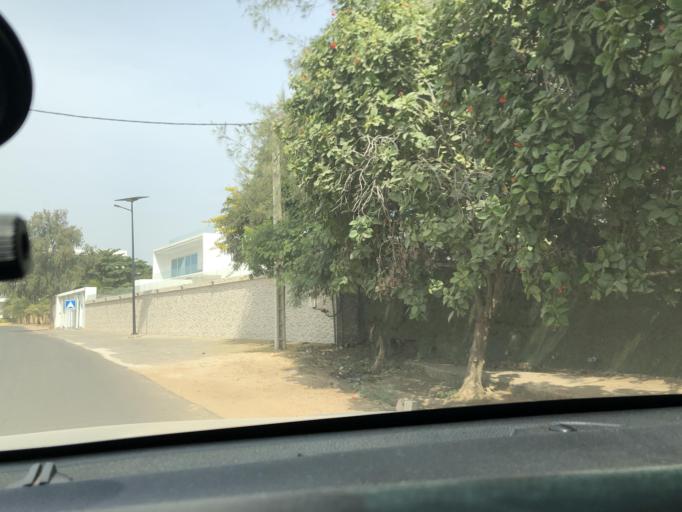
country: SN
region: Dakar
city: Mermoz Boabab
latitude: 14.7333
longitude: -17.5093
